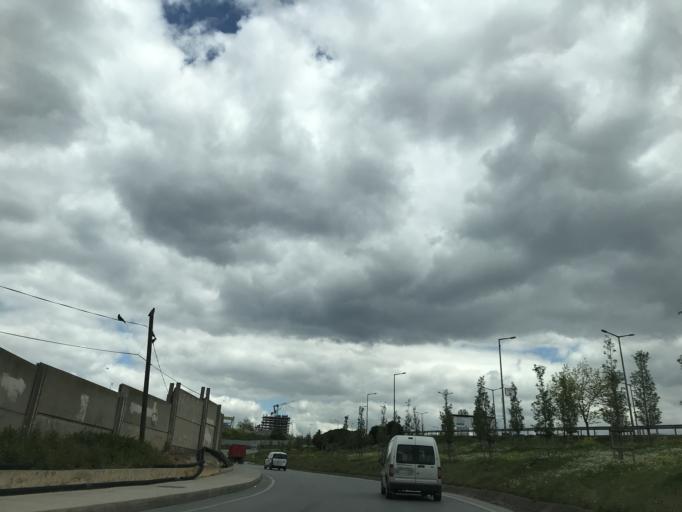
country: TR
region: Istanbul
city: Maltepe
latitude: 40.9029
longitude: 29.2076
